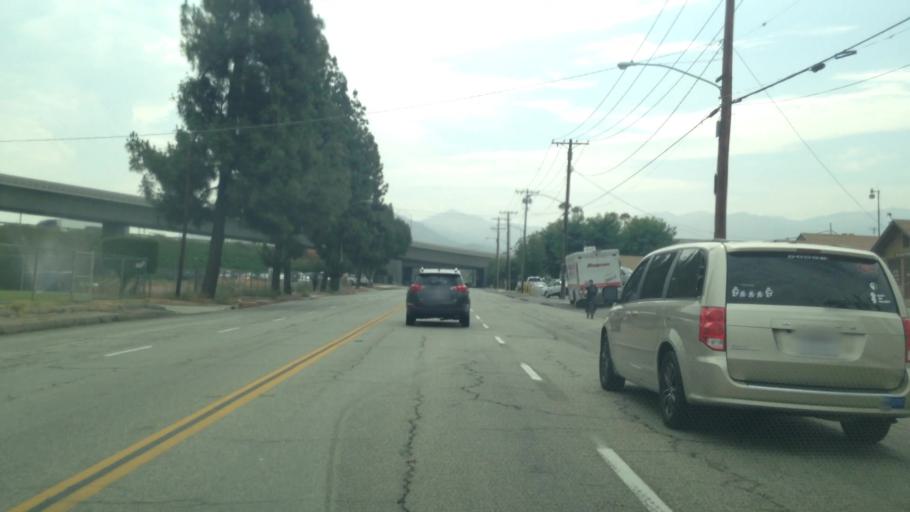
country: US
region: California
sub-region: Riverside County
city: Highgrove
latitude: 33.9903
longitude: -117.3543
